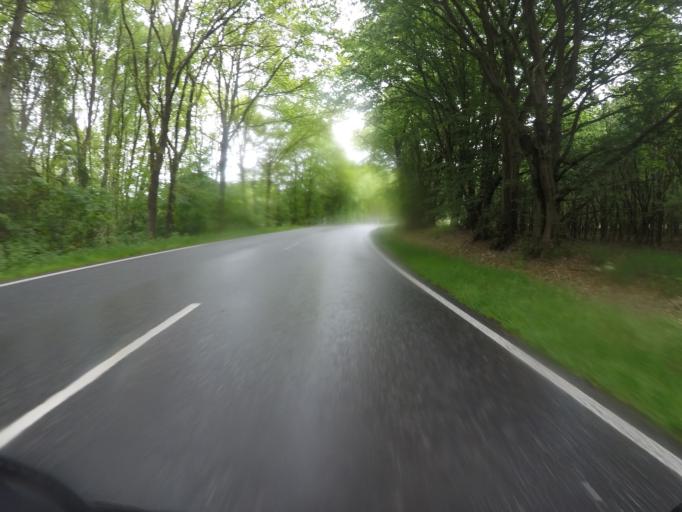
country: DE
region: Schleswig-Holstein
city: Heidmuhlen
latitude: 53.9497
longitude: 10.0848
